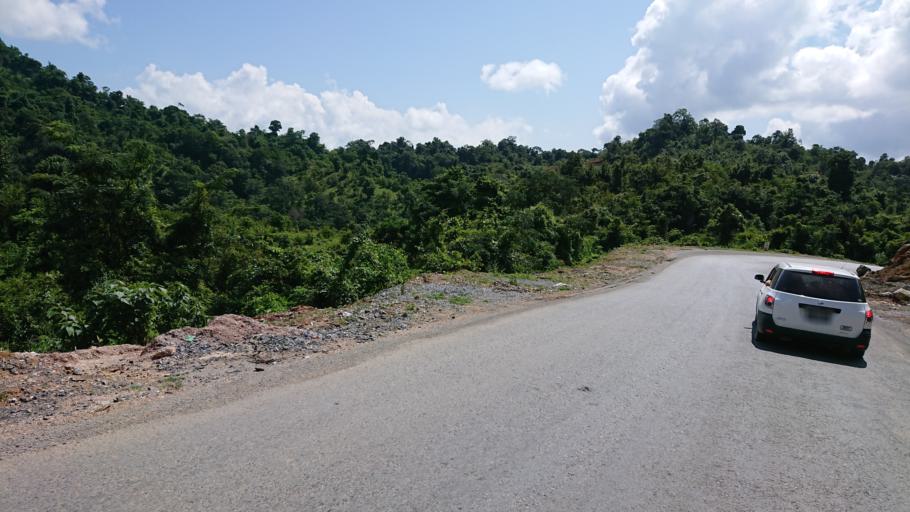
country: MM
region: Shan
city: Taunggyi
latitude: 20.8178
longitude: 97.3152
